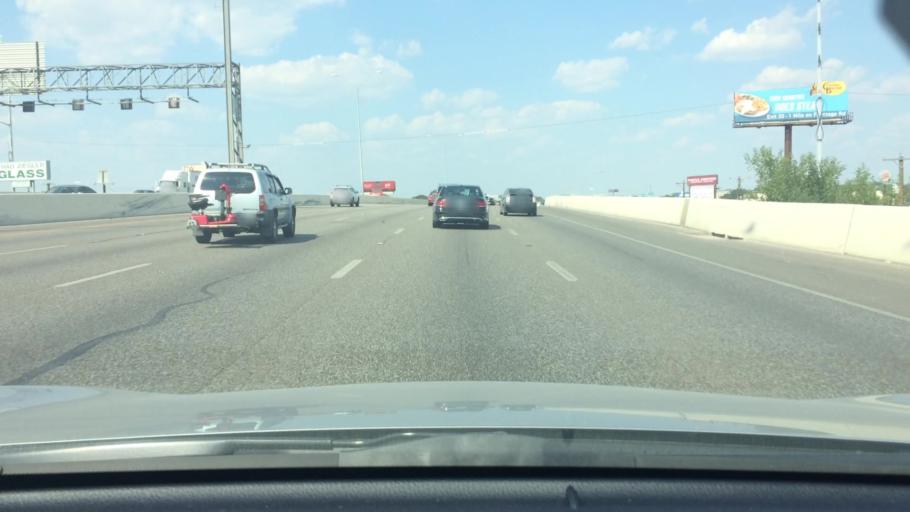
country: US
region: Texas
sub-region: Bexar County
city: Castle Hills
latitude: 29.5154
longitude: -98.5295
